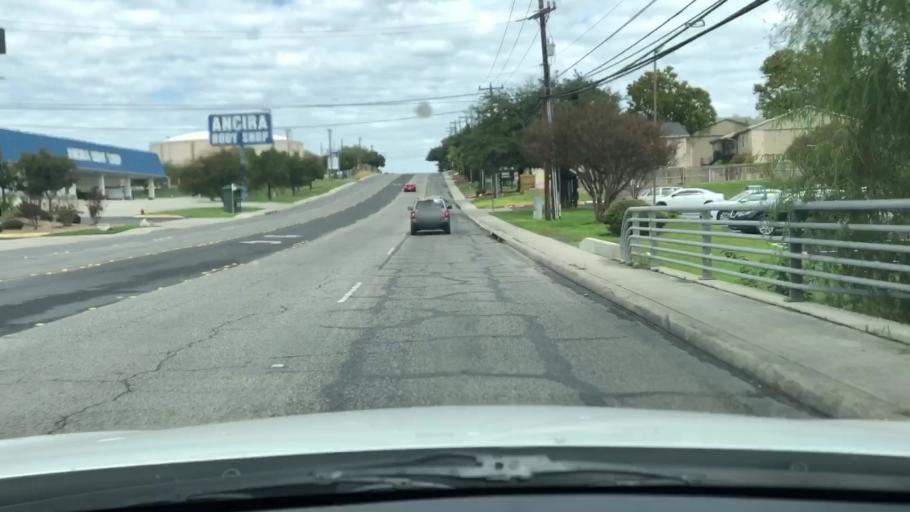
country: US
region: Texas
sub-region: Bexar County
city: Leon Valley
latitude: 29.4863
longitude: -98.6029
